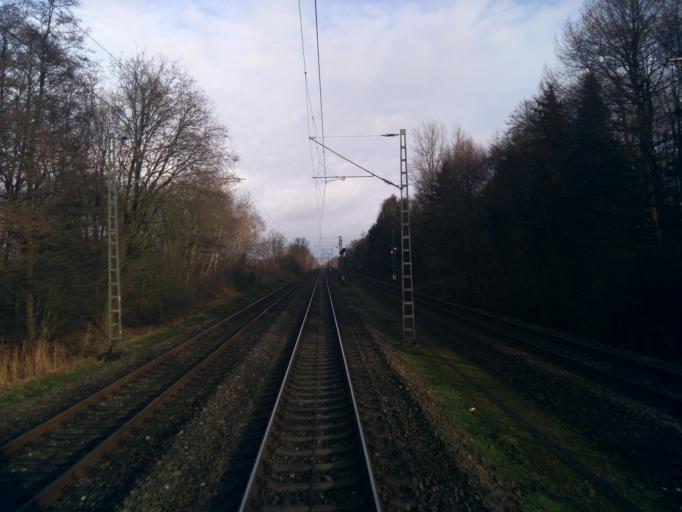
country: DE
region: Lower Saxony
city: Vahlde
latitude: 53.2190
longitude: 9.6174
